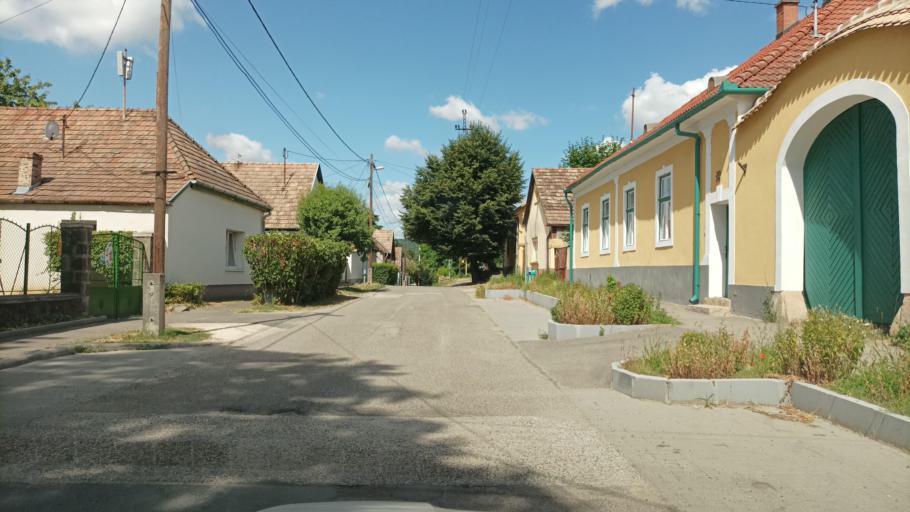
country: HU
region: Pest
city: Kismaros
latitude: 47.8083
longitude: 19.0046
